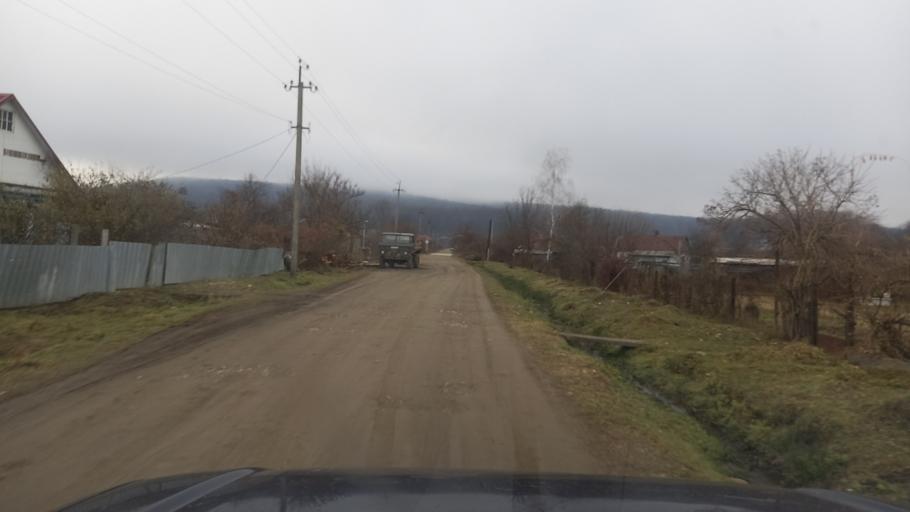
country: RU
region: Krasnodarskiy
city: Neftegorsk
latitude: 44.2492
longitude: 39.7643
